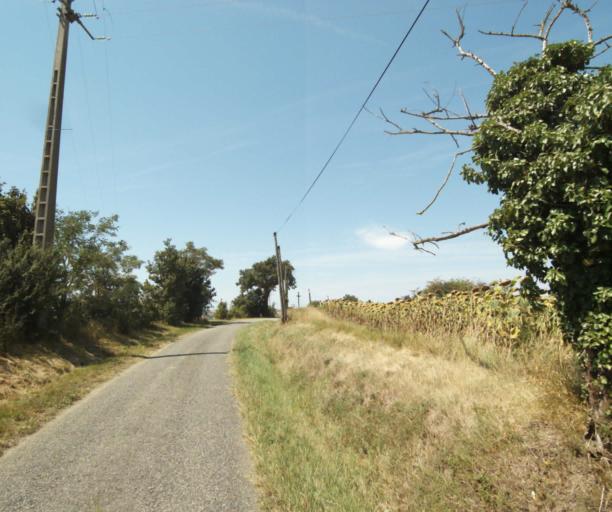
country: FR
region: Midi-Pyrenees
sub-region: Departement de l'Ariege
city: Lezat-sur-Leze
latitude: 43.3075
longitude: 1.3522
